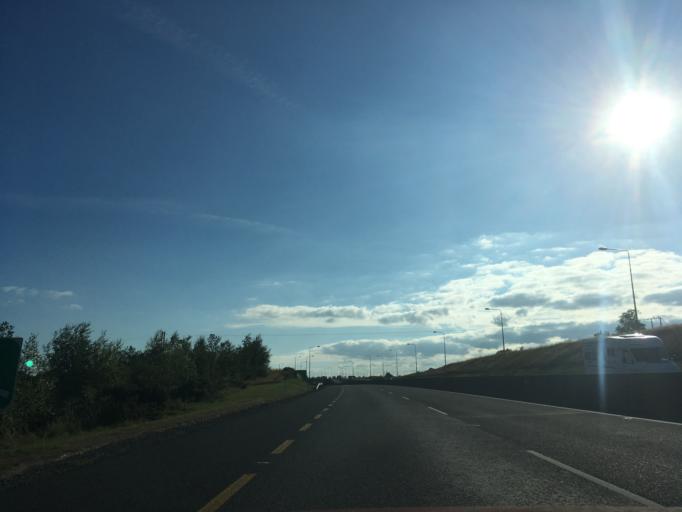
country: IE
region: Munster
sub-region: Waterford
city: Waterford
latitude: 52.2859
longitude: -7.1378
